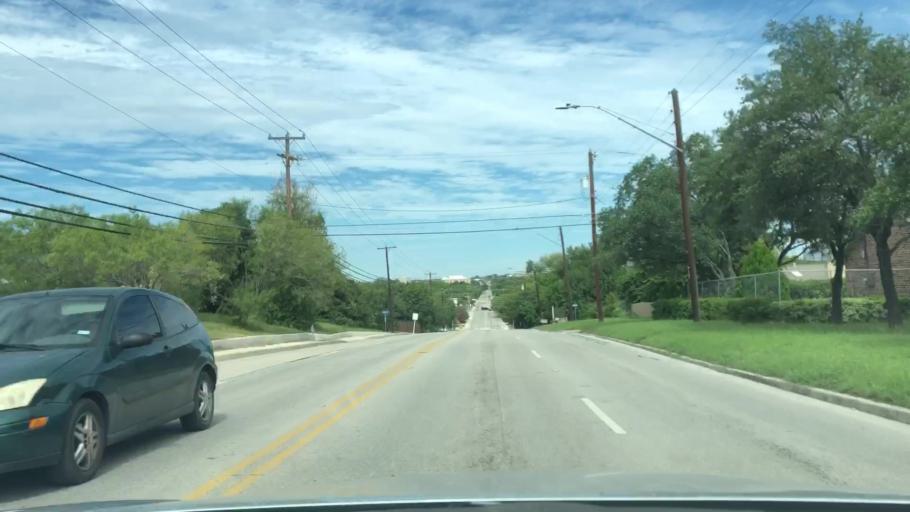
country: US
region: Texas
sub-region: Bexar County
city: Olmos Park
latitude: 29.5004
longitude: -98.4917
